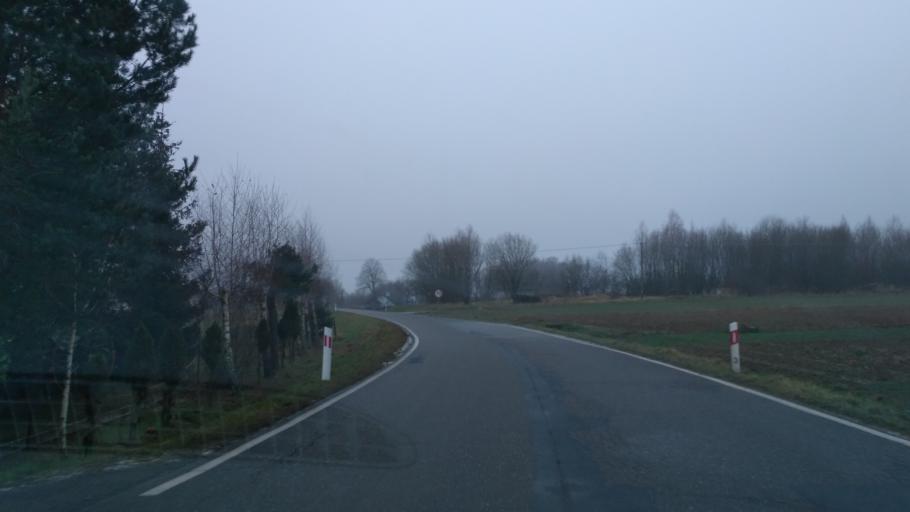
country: PL
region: Subcarpathian Voivodeship
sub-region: Powiat lancucki
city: Handzlowka
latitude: 49.9656
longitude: 22.1917
